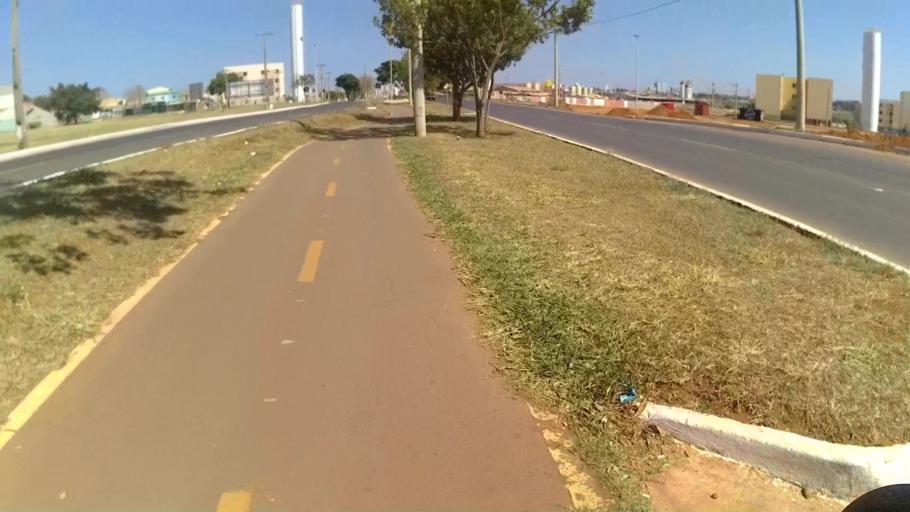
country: BR
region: Federal District
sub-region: Brasilia
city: Brasilia
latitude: -15.8941
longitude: -48.0451
